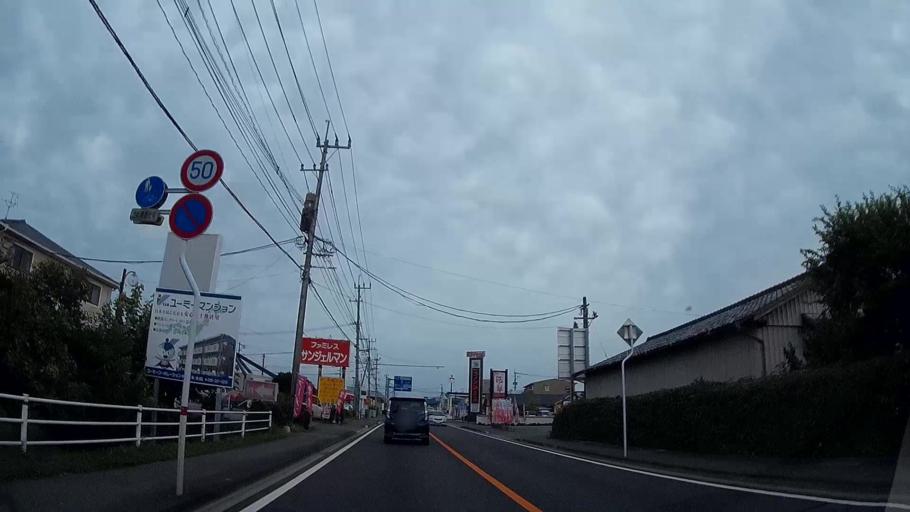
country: JP
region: Kumamoto
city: Kikuchi
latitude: 32.9734
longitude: 130.8090
